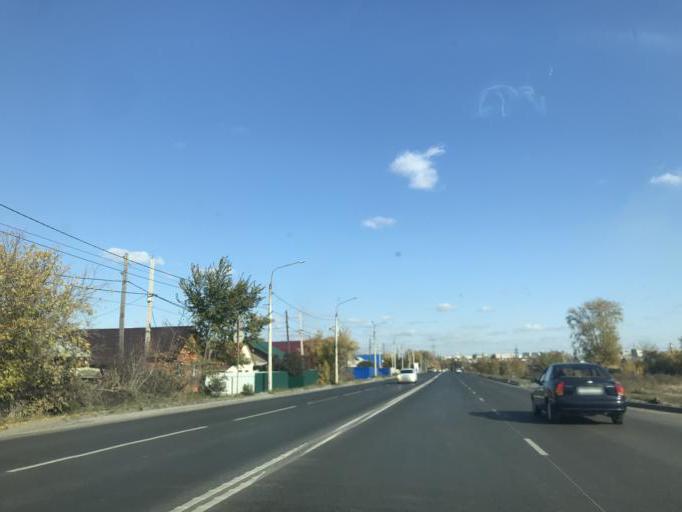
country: RU
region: Chelyabinsk
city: Dolgoderevenskoye
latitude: 55.2405
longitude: 61.3501
